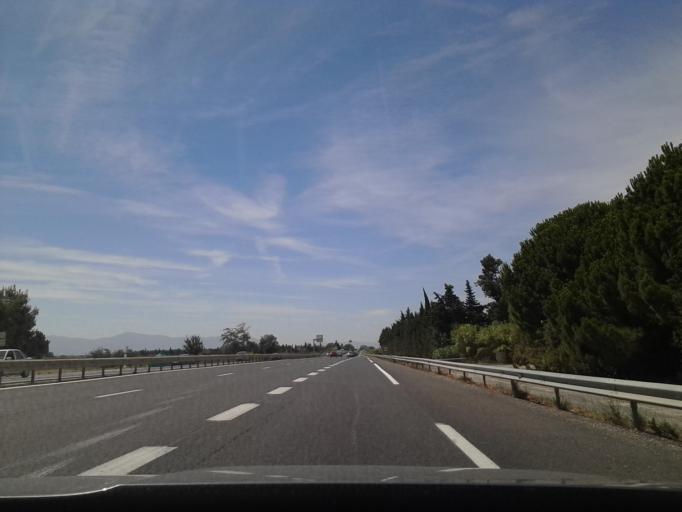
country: FR
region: Languedoc-Roussillon
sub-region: Departement des Pyrenees-Orientales
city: Rivesaltes
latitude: 42.7779
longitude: 2.9029
